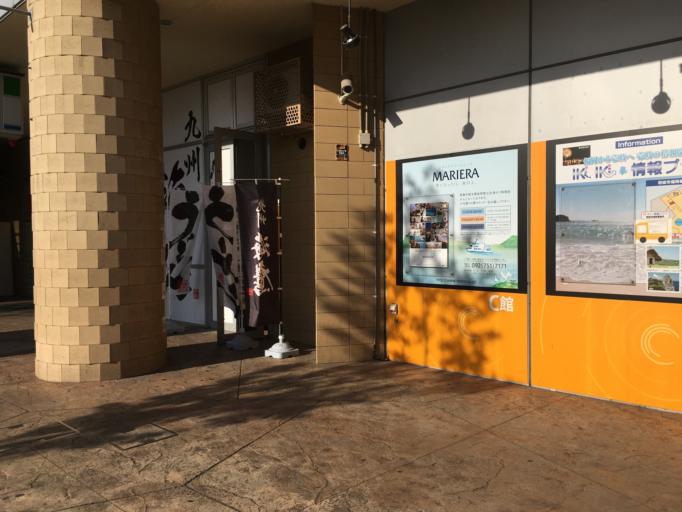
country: JP
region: Fukuoka
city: Fukuoka-shi
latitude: 33.6043
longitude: 130.3985
